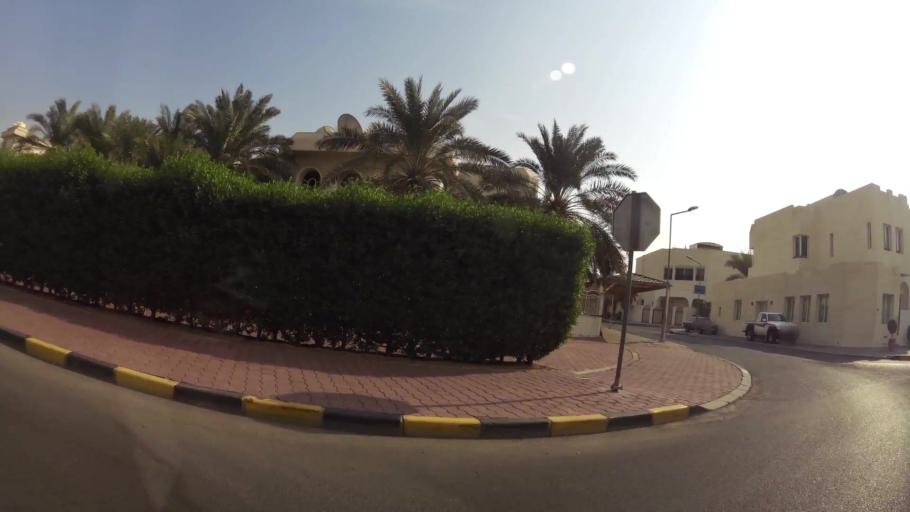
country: KW
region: Al Farwaniyah
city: Janub as Surrah
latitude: 29.3100
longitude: 47.9841
